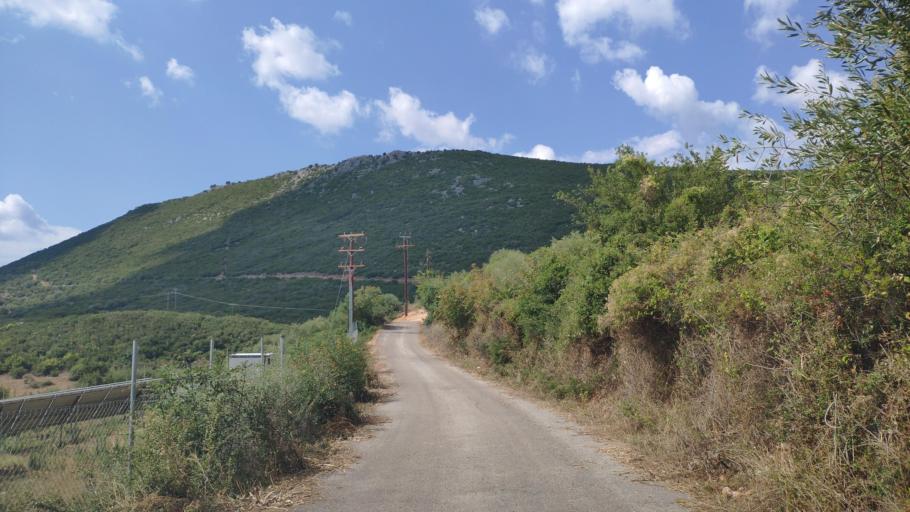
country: GR
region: West Greece
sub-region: Nomos Aitolias kai Akarnanias
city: Fitiai
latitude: 38.6705
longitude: 21.1450
